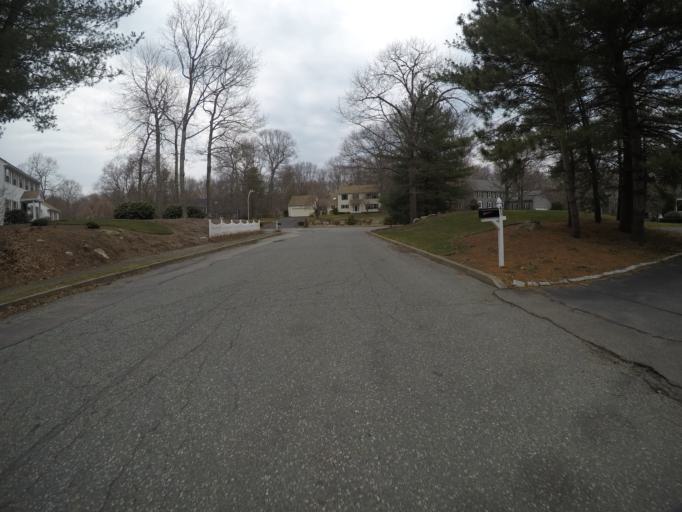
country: US
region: Massachusetts
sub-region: Norfolk County
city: Stoughton
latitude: 42.0833
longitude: -71.1088
